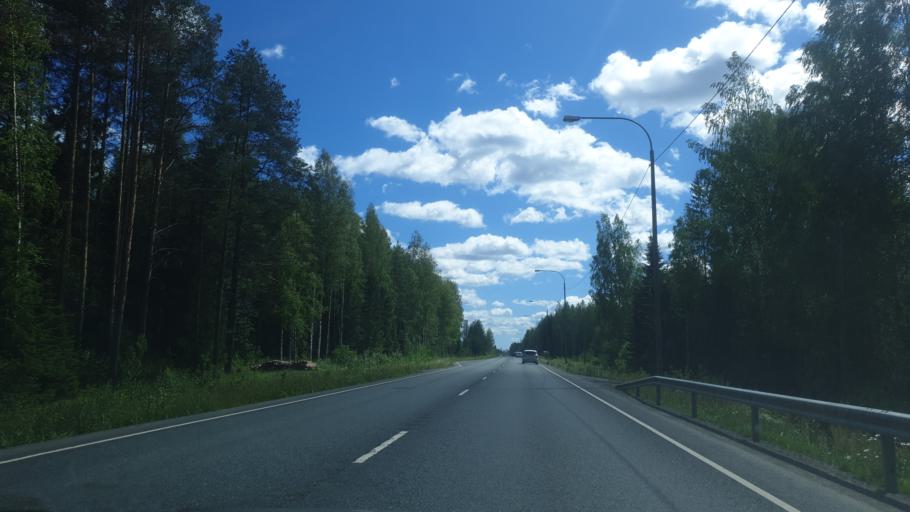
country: FI
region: Northern Savo
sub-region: Varkaus
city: Leppaevirta
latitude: 62.5229
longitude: 27.6733
